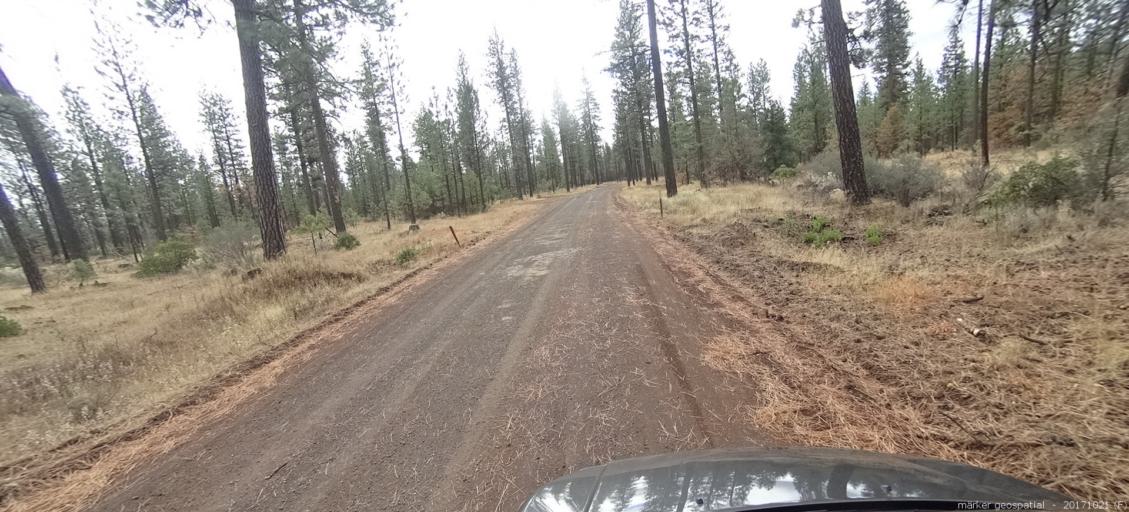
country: US
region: California
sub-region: Shasta County
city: Burney
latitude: 40.9897
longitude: -121.6332
